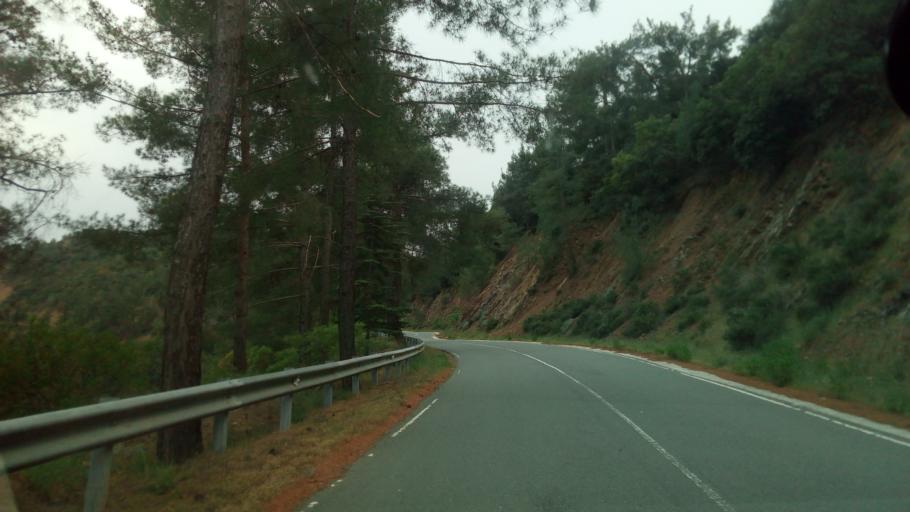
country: CY
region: Lefkosia
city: Kakopetria
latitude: 34.9830
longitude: 32.7532
